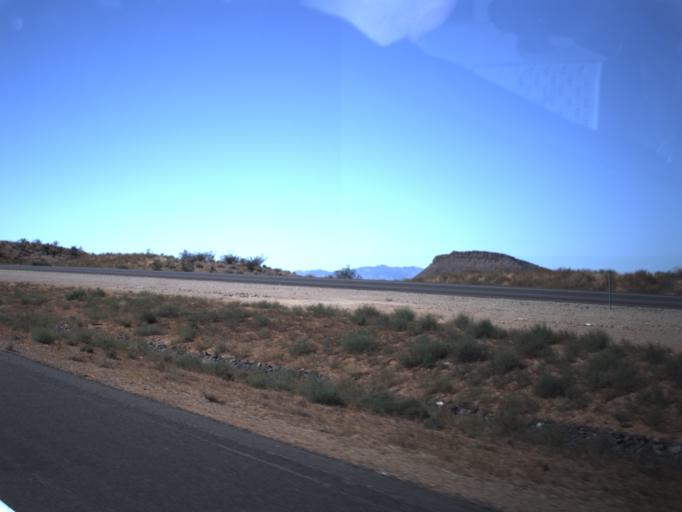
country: US
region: Utah
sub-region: Washington County
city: Washington
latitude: 37.1124
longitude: -113.4580
